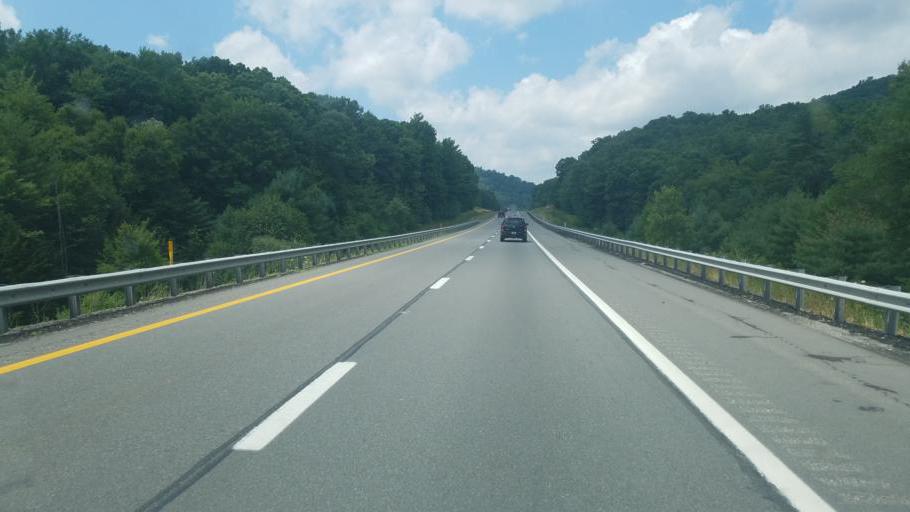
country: US
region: West Virginia
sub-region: Raleigh County
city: Shady Spring
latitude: 37.7027
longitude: -81.1422
